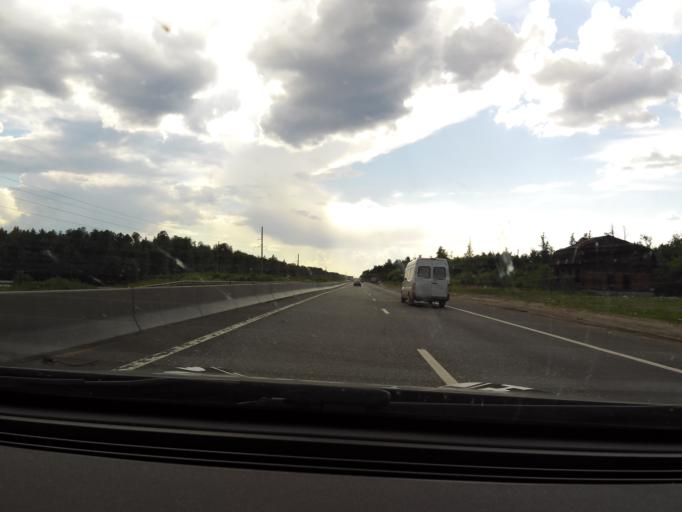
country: RU
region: Nizjnij Novgorod
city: Smolino
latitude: 56.2834
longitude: 43.1290
